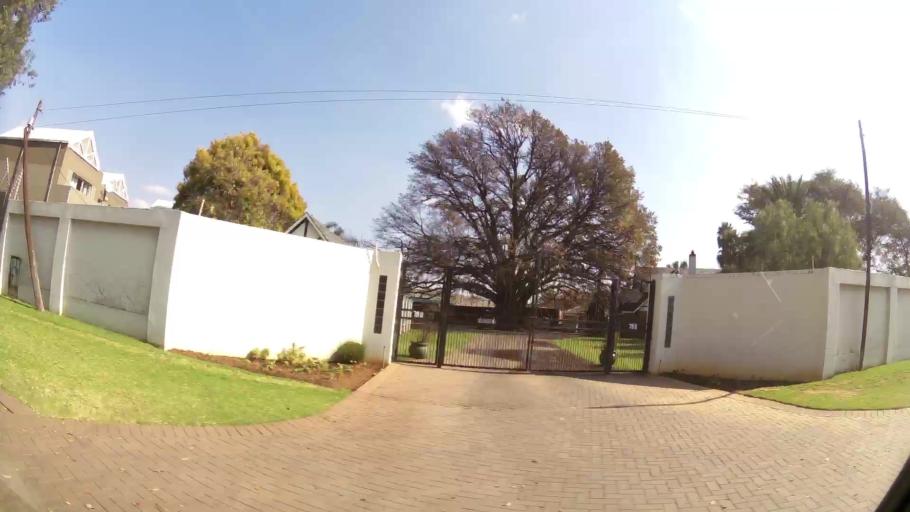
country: ZA
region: Gauteng
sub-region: Ekurhuleni Metropolitan Municipality
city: Boksburg
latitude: -26.1862
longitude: 28.2848
